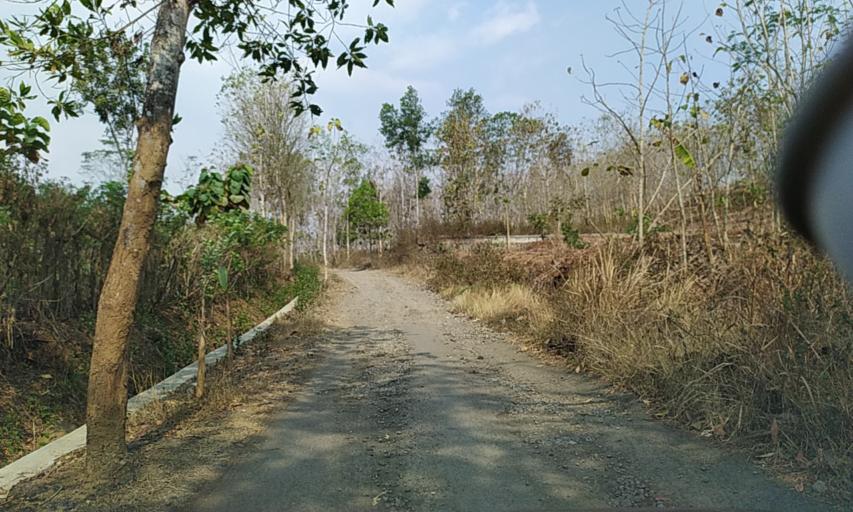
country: ID
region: Central Java
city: Karanggintung
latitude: -7.4688
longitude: 108.8869
